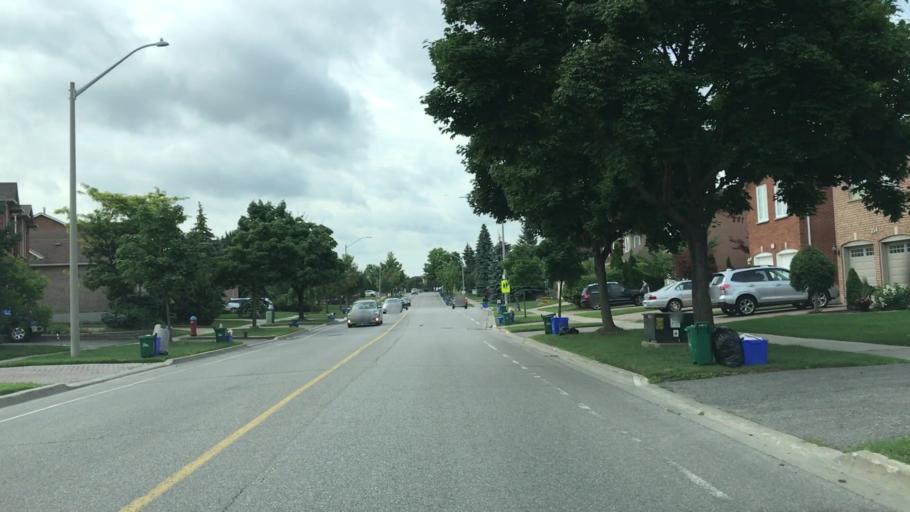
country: CA
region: Ontario
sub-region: York
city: Richmond Hill
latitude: 43.8543
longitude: -79.4015
